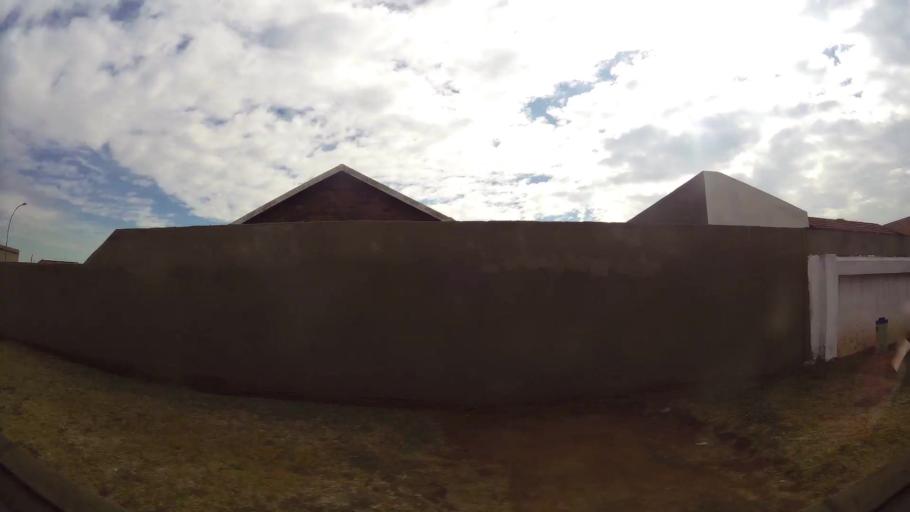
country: ZA
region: Gauteng
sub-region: Ekurhuleni Metropolitan Municipality
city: Germiston
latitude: -26.3248
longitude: 28.1765
